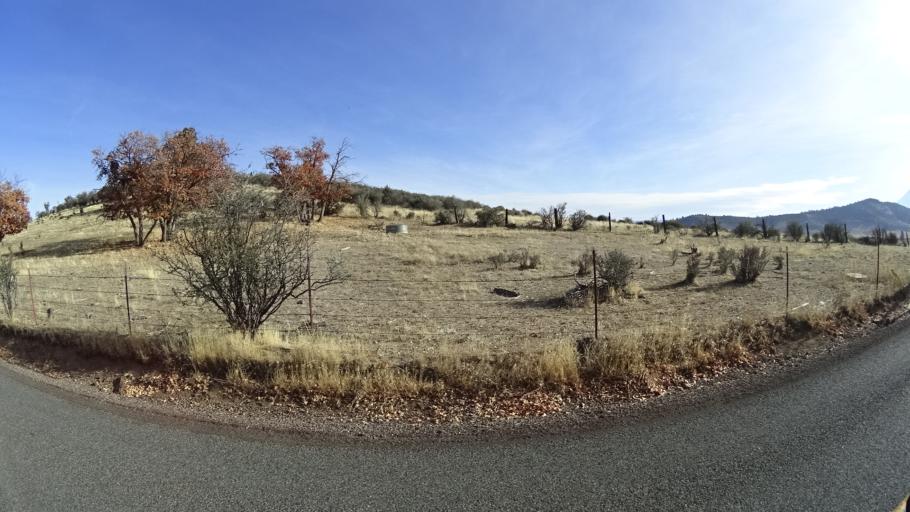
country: US
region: California
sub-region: Siskiyou County
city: Montague
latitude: 41.6440
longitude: -122.5786
